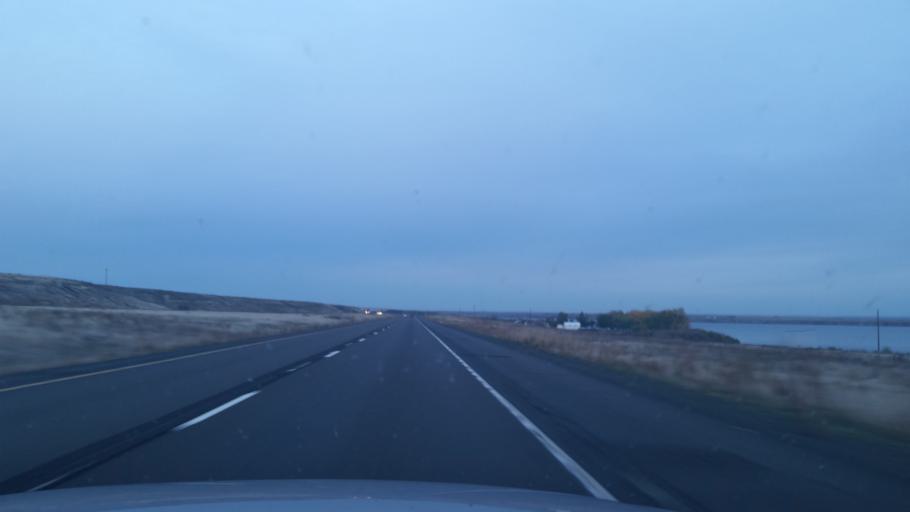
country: US
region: Washington
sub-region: Adams County
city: Ritzville
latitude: 47.2532
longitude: -118.0960
